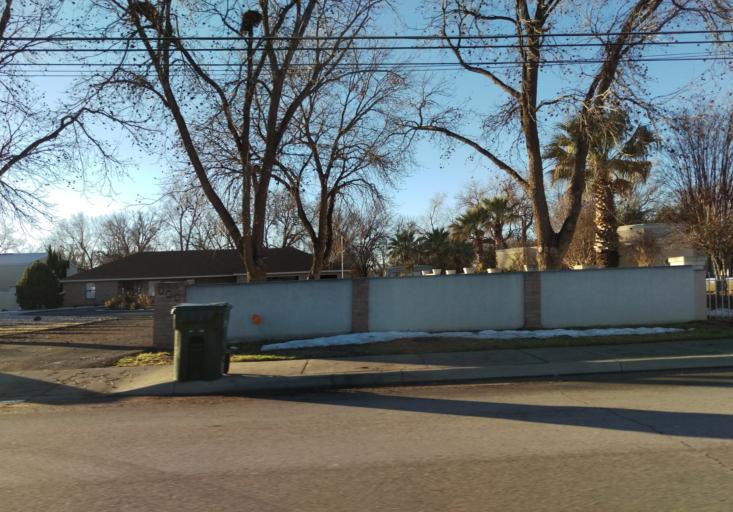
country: US
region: New Mexico
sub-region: Eddy County
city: La Huerta
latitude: 32.4428
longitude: -104.2295
